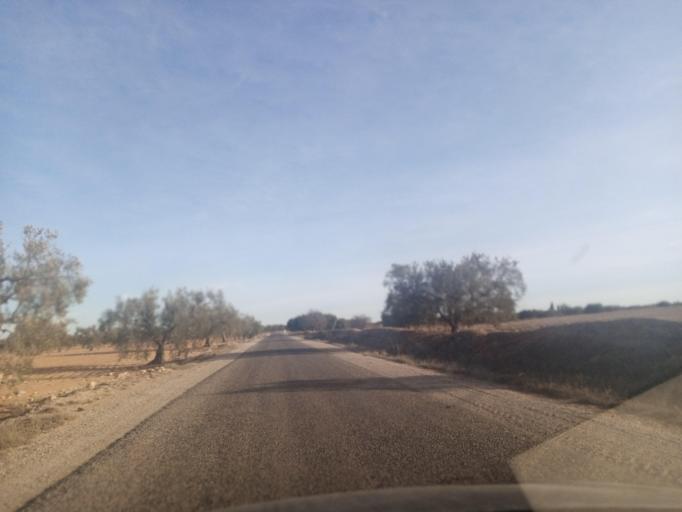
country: TN
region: Safaqis
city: Bi'r `Ali Bin Khalifah
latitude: 34.8891
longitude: 10.1793
